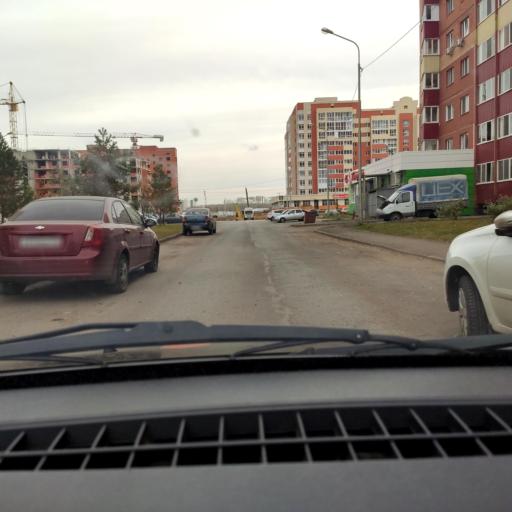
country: RU
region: Bashkortostan
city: Mikhaylovka
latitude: 54.7135
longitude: 55.8413
